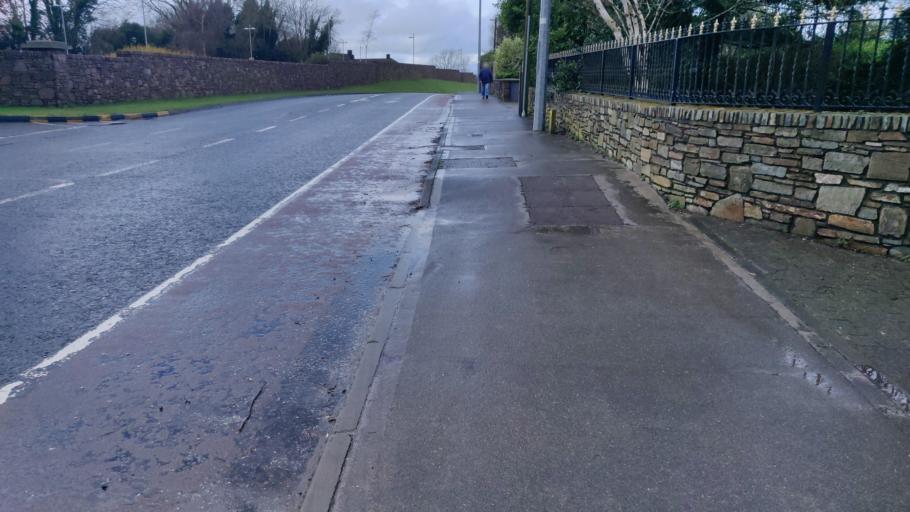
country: IE
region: Munster
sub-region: County Cork
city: Cork
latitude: 51.8706
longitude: -8.4183
